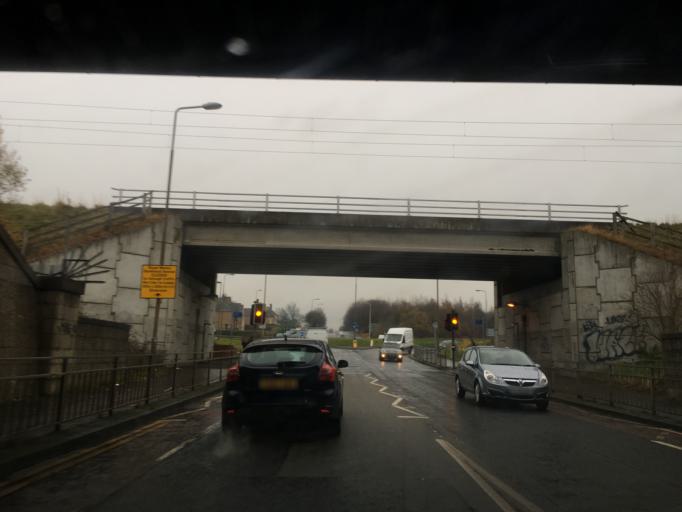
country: GB
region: Scotland
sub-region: Edinburgh
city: Colinton
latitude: 55.9304
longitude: -3.2859
